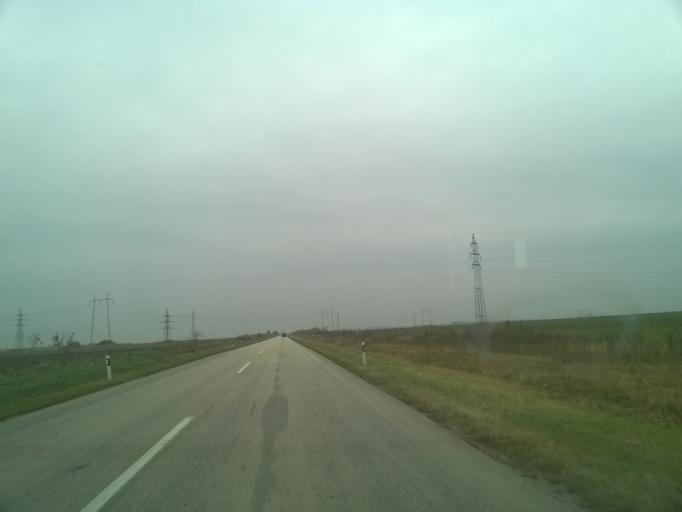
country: RS
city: Crepaja
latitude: 44.9632
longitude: 20.6553
